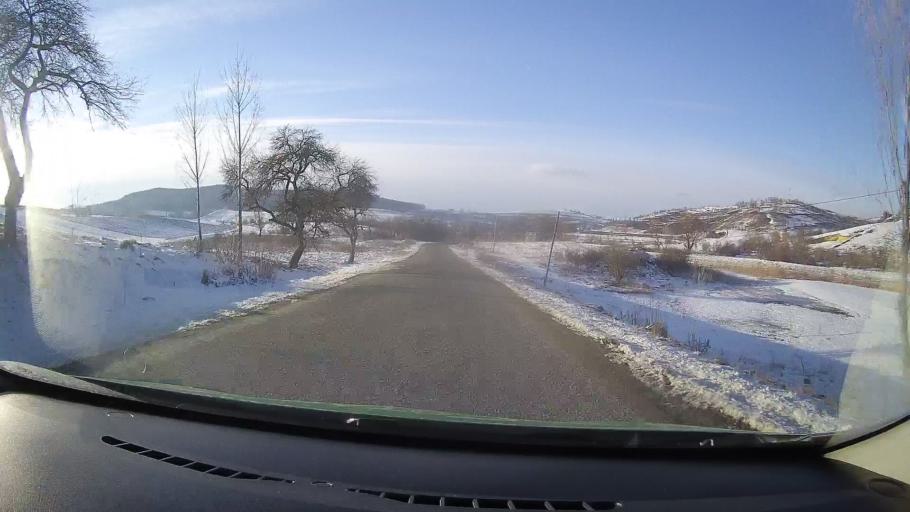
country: RO
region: Sibiu
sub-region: Comuna Merghindeal
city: Merghindeal
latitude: 45.9705
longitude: 24.7091
